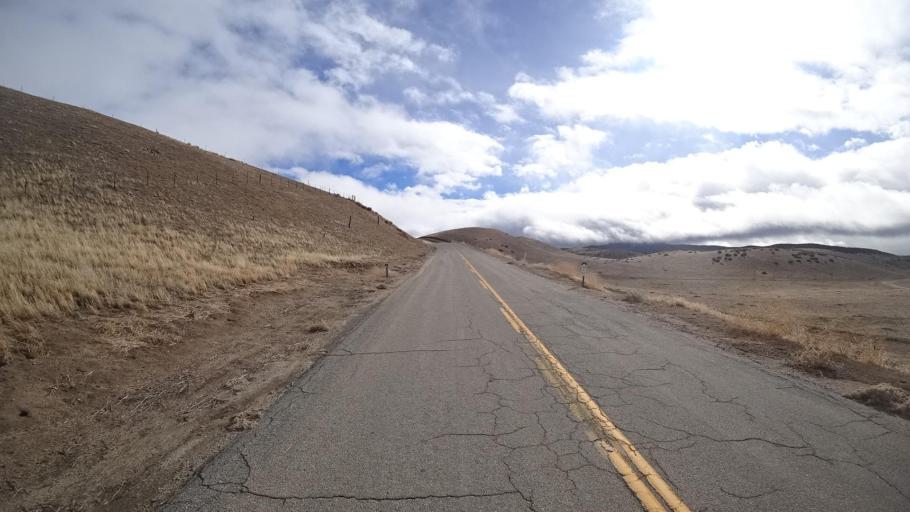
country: US
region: California
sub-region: Kern County
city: Maricopa
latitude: 34.9028
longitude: -119.3736
